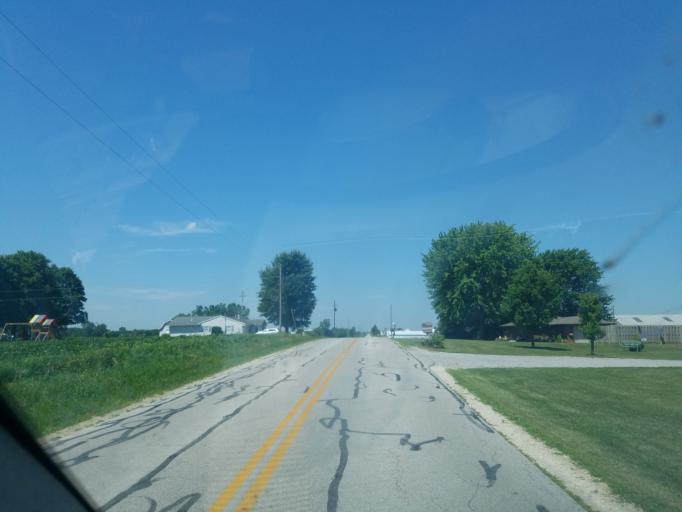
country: US
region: Ohio
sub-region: Mercer County
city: Saint Henry
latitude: 40.4506
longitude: -84.6996
